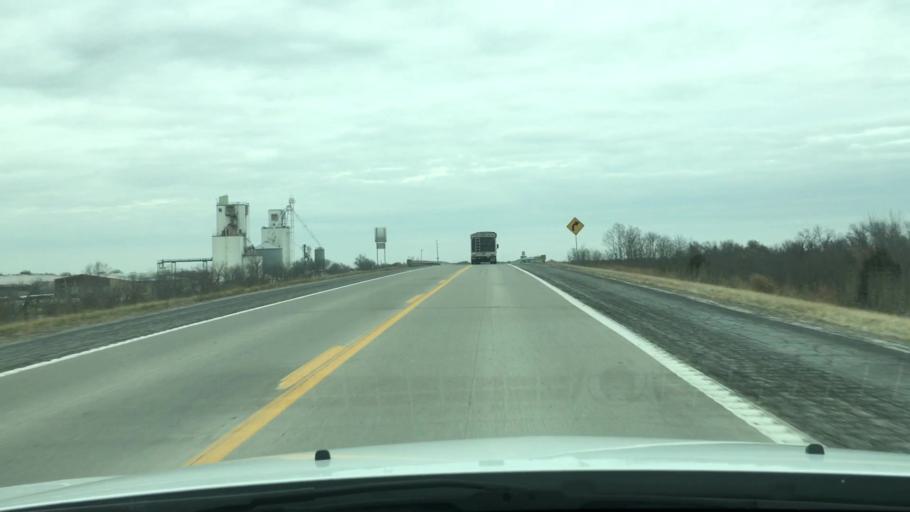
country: US
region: Missouri
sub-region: Audrain County
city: Mexico
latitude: 39.1556
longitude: -91.8431
